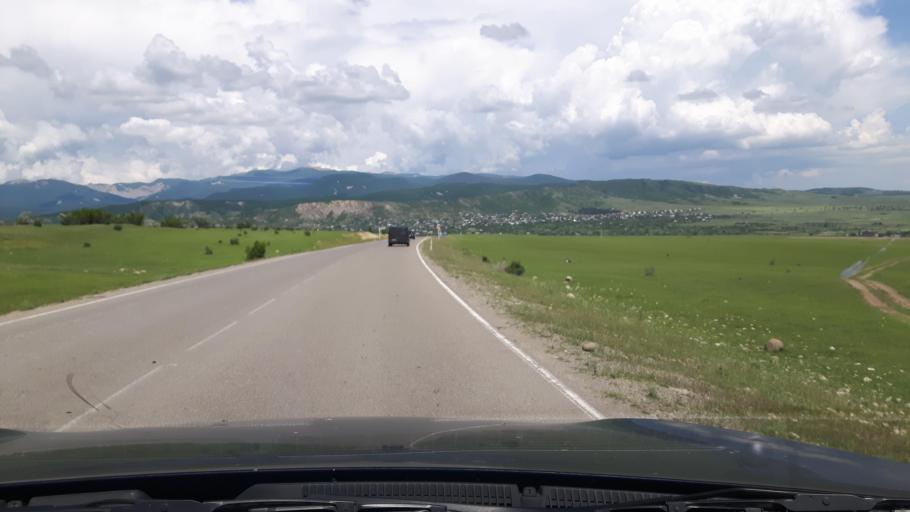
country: GE
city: Didi Lilo
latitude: 41.7527
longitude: 45.1461
